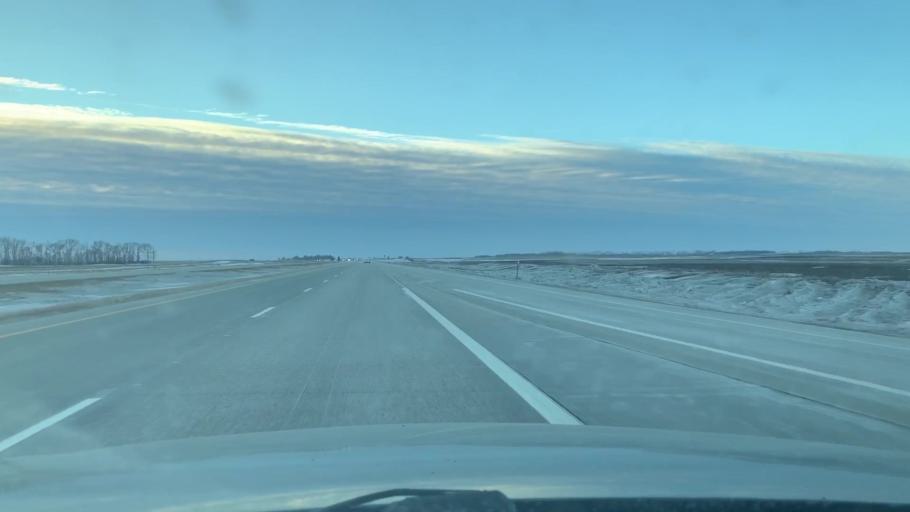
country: US
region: North Dakota
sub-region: Cass County
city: Casselton
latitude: 46.8758
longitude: -97.4971
